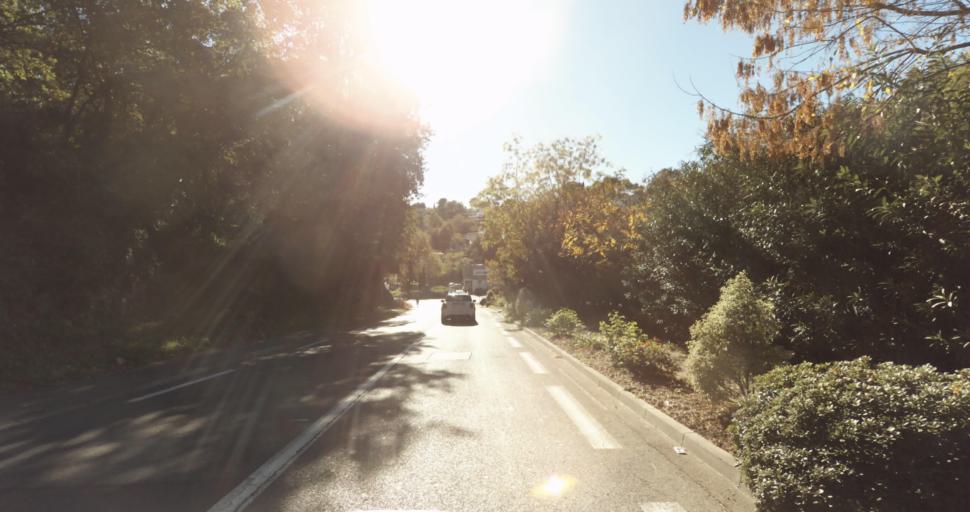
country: FR
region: Provence-Alpes-Cote d'Azur
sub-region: Departement des Alpes-Maritimes
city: Vence
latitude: 43.7184
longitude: 7.1136
